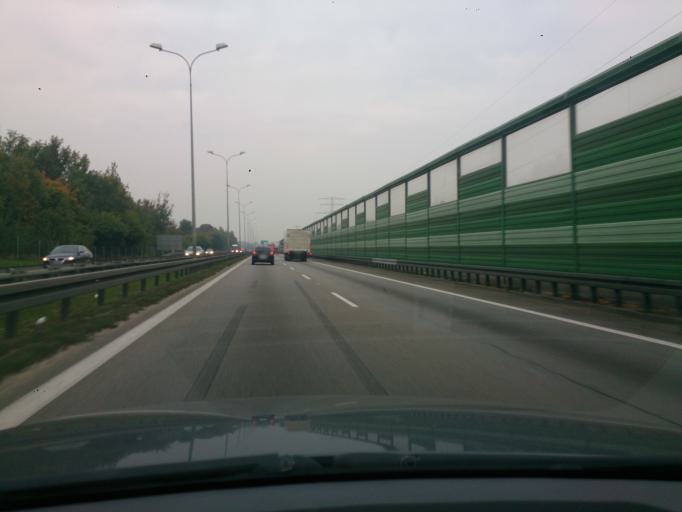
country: PL
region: Pomeranian Voivodeship
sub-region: Gdynia
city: Wielki Kack
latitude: 54.4194
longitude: 18.4869
